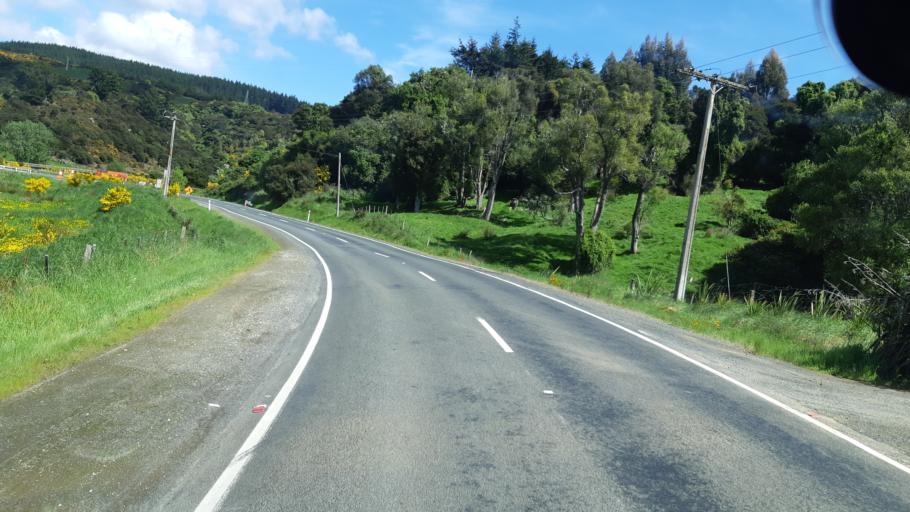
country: NZ
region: Otago
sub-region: Dunedin City
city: Portobello
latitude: -45.7159
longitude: 170.5728
